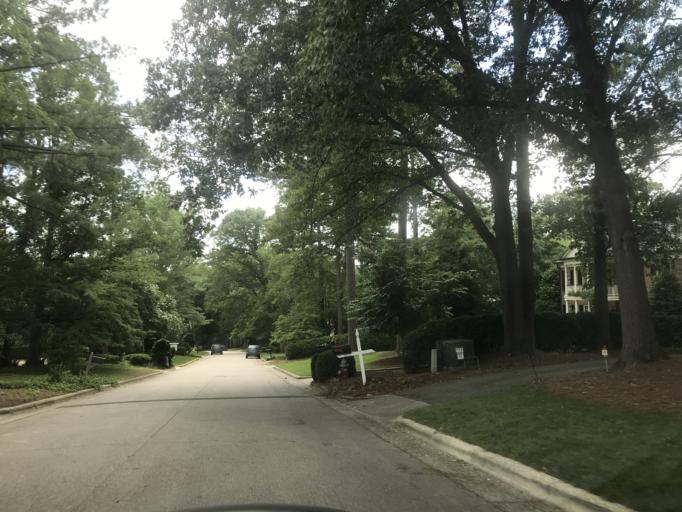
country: US
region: North Carolina
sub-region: Wake County
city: West Raleigh
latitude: 35.8308
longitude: -78.6520
